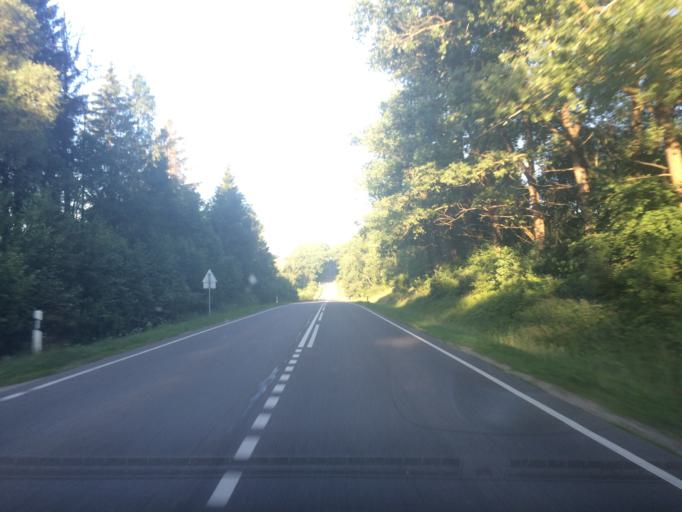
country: LT
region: Utenos apskritis
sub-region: Anyksciai
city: Anyksciai
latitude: 55.3991
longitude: 25.0899
